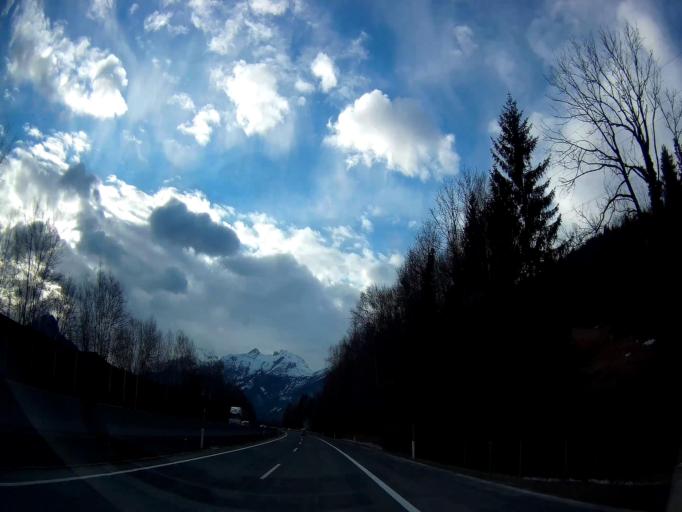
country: AT
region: Salzburg
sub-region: Politischer Bezirk Hallein
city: Kuchl
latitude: 47.6271
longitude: 13.1328
